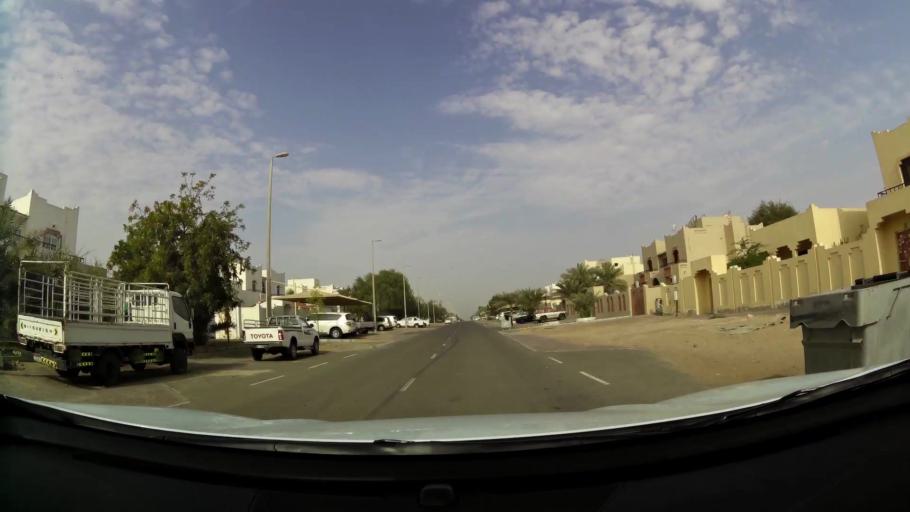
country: AE
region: Abu Dhabi
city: Abu Dhabi
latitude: 24.2382
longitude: 54.7250
